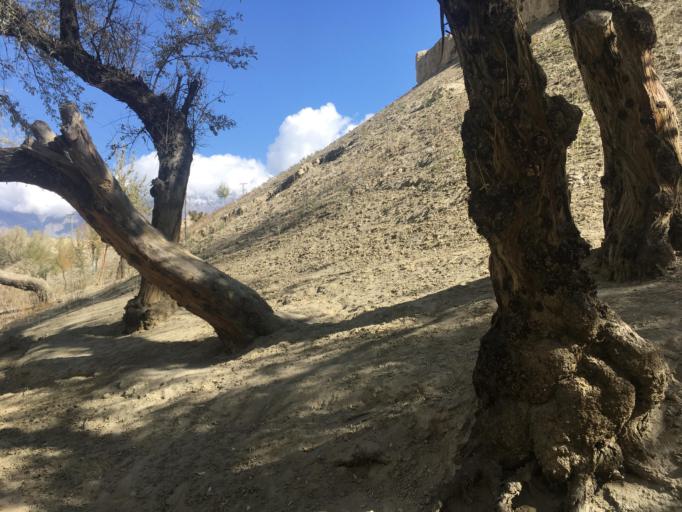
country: PK
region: Gilgit-Baltistan
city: Skardu
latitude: 35.3329
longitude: 75.5209
